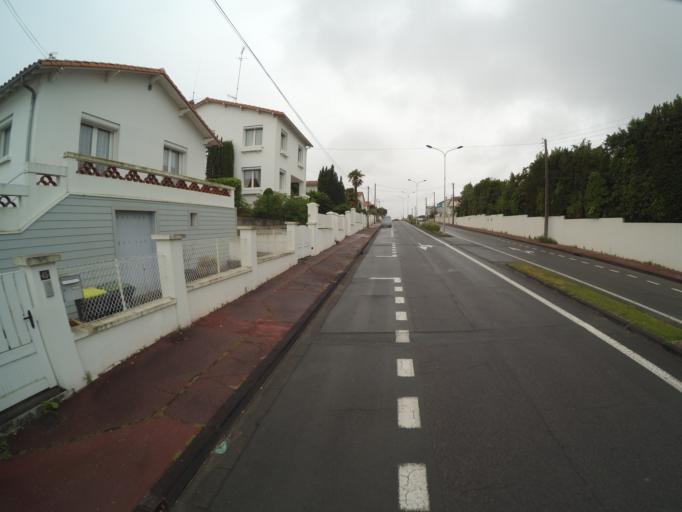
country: FR
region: Poitou-Charentes
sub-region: Departement de la Charente-Maritime
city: Saint-Georges-de-Didonne
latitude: 45.6199
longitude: -1.0075
